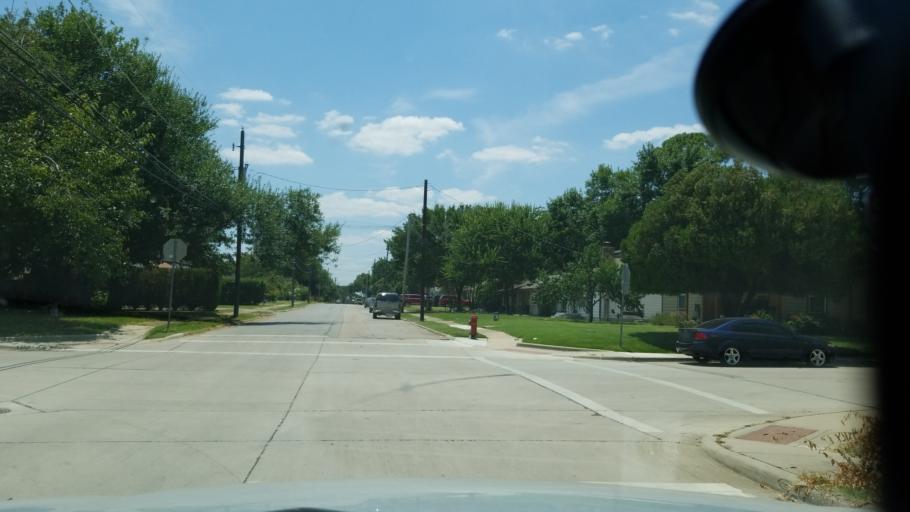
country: US
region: Texas
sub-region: Dallas County
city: Grand Prairie
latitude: 32.7531
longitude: -96.9617
